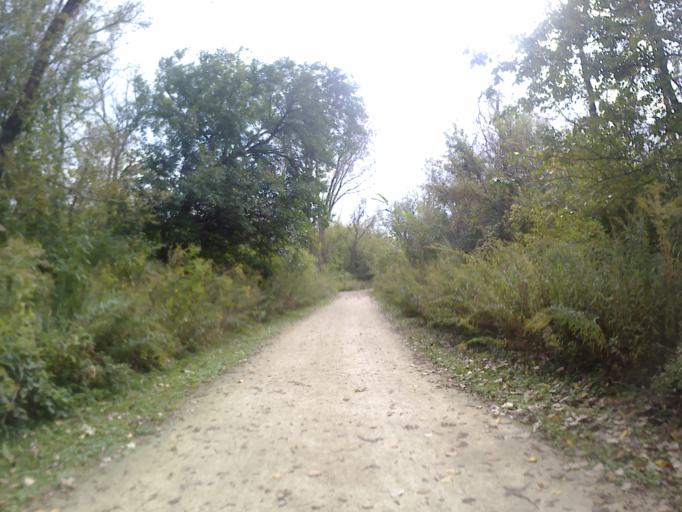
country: US
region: Illinois
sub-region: DuPage County
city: Naperville
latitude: 41.7830
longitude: -88.1766
